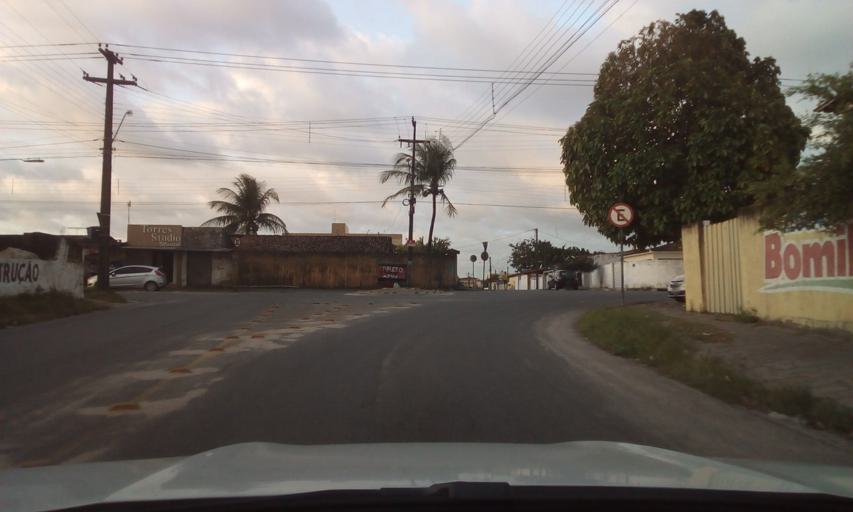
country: BR
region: Paraiba
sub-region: Joao Pessoa
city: Joao Pessoa
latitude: -7.1795
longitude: -34.8866
